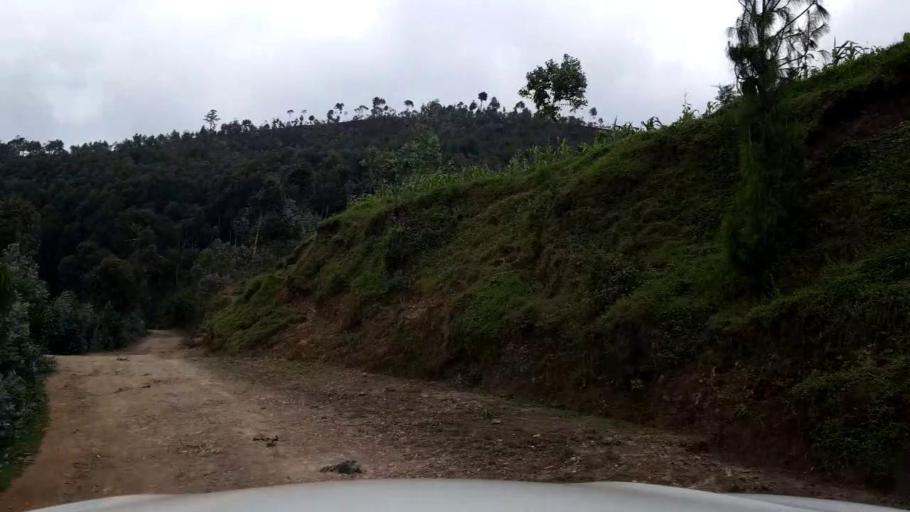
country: RW
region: Western Province
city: Kibuye
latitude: -1.9552
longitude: 29.4744
